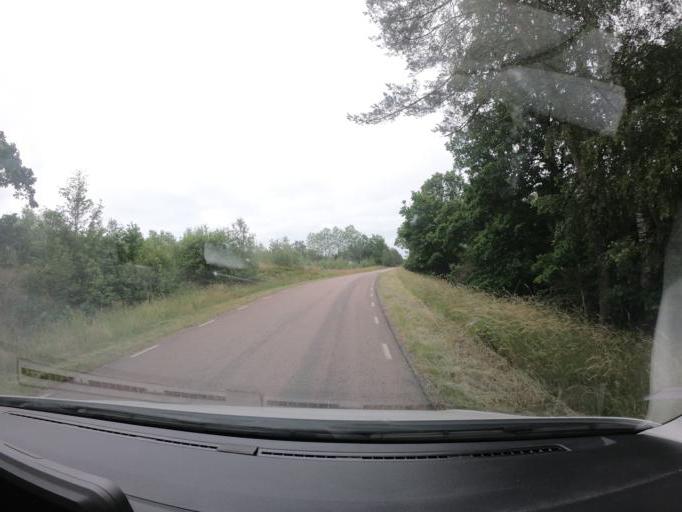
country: SE
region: Skane
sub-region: Perstorps Kommun
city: Perstorp
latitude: 56.0855
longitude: 13.3187
